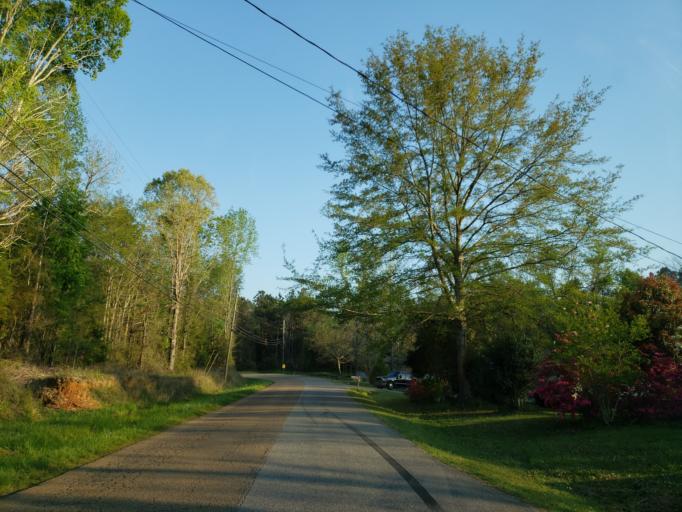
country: US
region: Mississippi
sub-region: Lauderdale County
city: Marion
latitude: 32.4000
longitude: -88.5898
